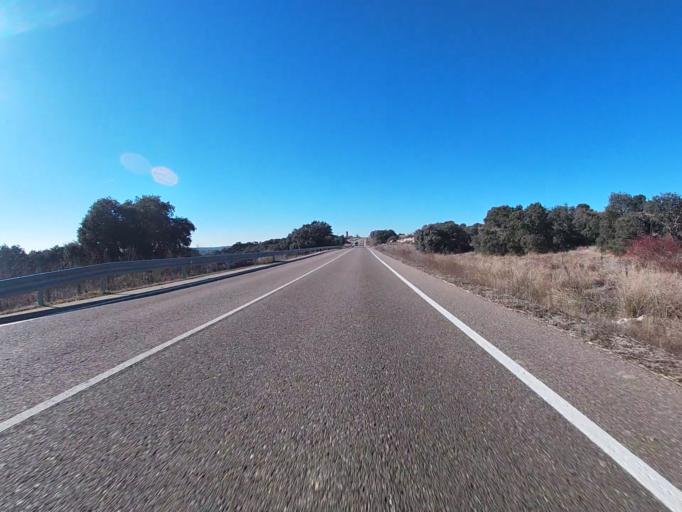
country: ES
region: Castille and Leon
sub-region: Provincia de Salamanca
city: Juzbado
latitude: 41.0778
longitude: -5.8508
